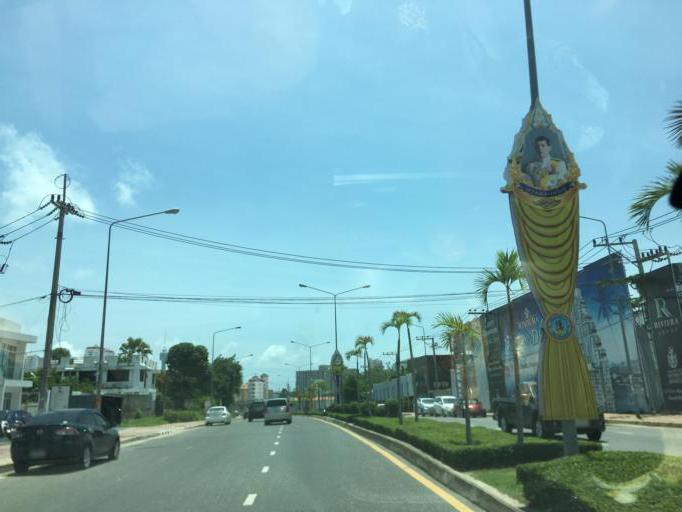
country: TH
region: Chon Buri
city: Phatthaya
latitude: 12.8939
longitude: 100.8765
